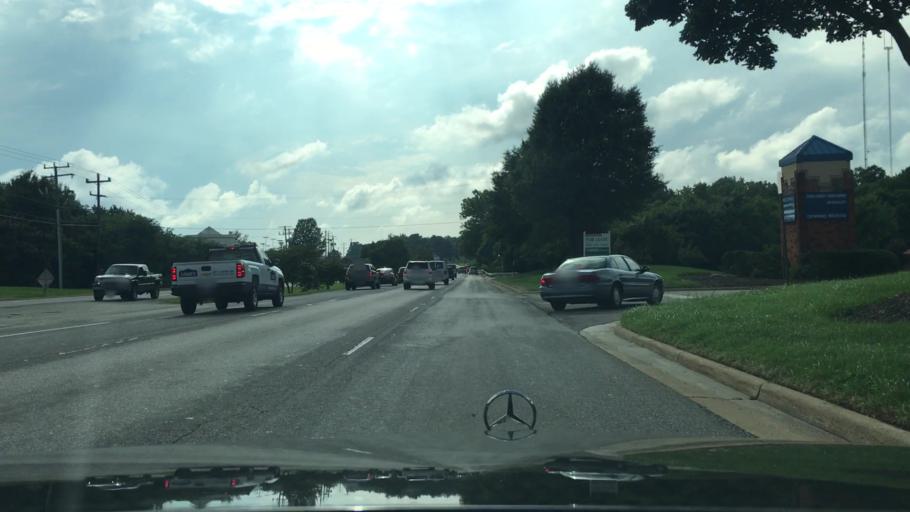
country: US
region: Virginia
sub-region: Chesterfield County
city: Bon Air
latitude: 37.5070
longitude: -77.5882
